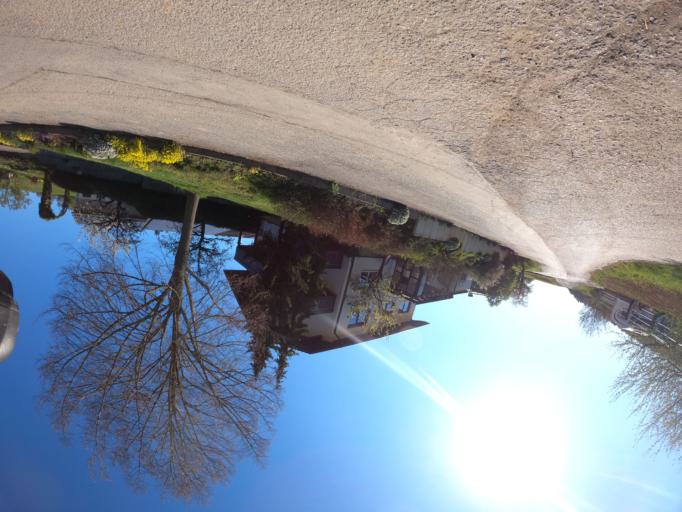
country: DE
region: Baden-Wuerttemberg
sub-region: Karlsruhe Region
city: Monsheim
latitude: 48.8705
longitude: 8.8640
